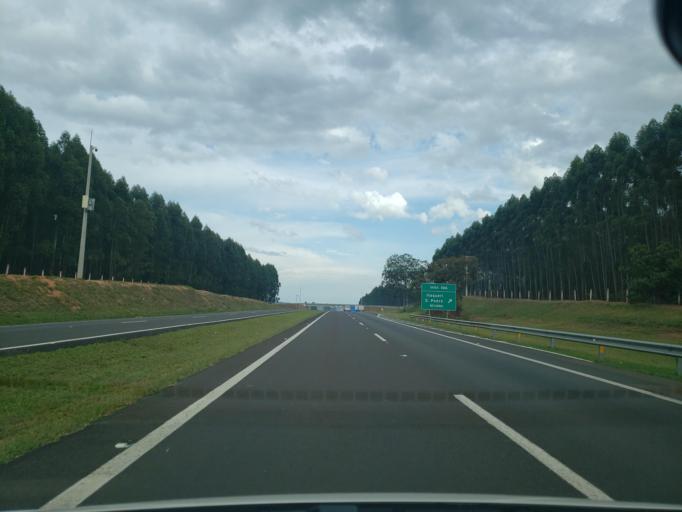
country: BR
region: Sao Paulo
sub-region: Itirapina
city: Itirapina
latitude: -22.2618
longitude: -47.8897
